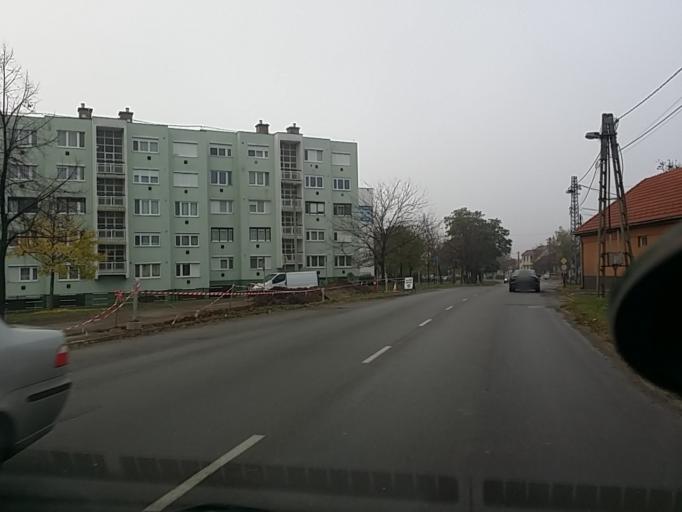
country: HU
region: Heves
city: Gyongyos
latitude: 47.7882
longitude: 19.9351
